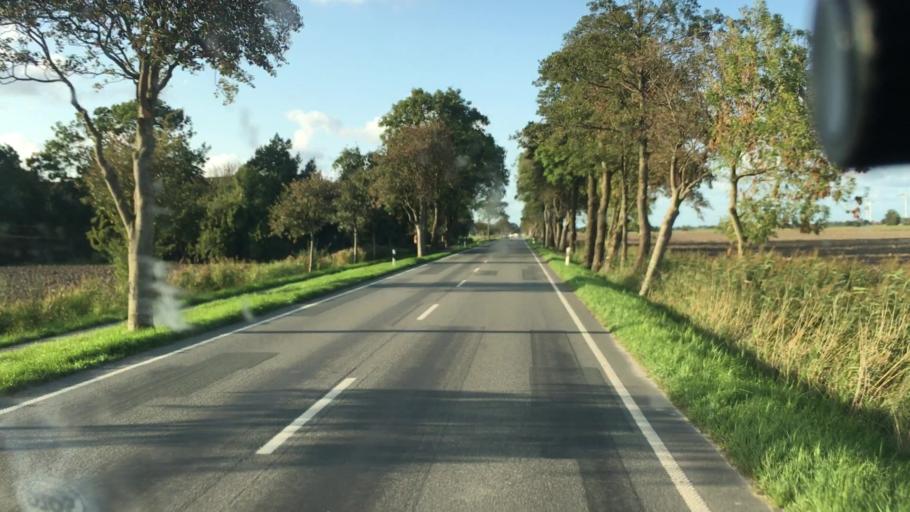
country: DE
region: Lower Saxony
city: Wittmund
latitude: 53.6426
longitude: 7.7903
